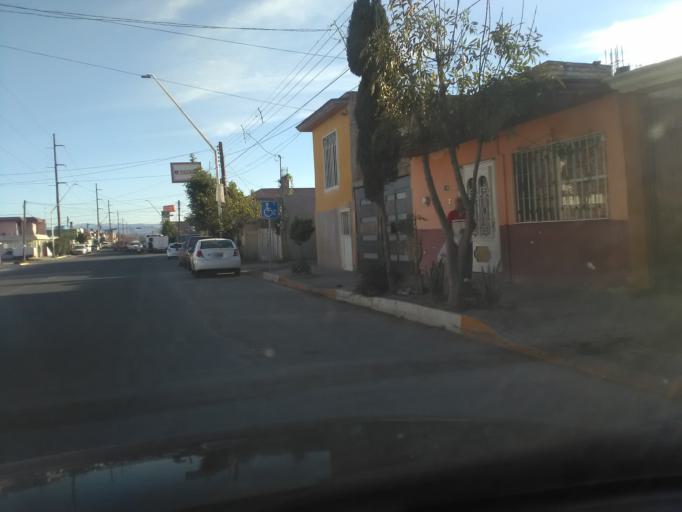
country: MX
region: Durango
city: Victoria de Durango
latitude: 24.0219
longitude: -104.6330
